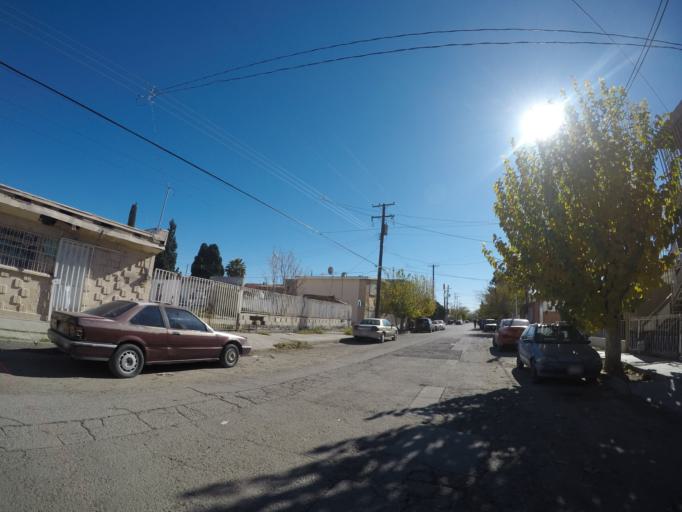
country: MX
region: Chihuahua
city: Ciudad Juarez
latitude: 31.7411
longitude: -106.4610
